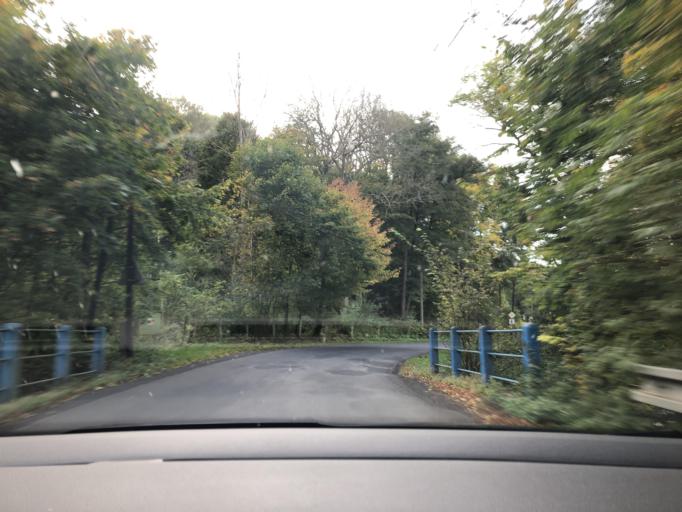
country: CZ
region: Ustecky
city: Velke Brezno
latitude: 50.6409
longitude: 14.1529
